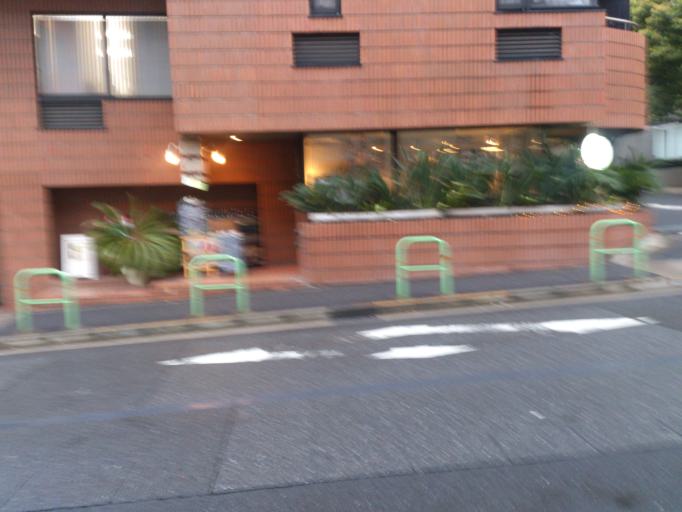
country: JP
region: Tokyo
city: Tokyo
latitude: 35.6702
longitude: 139.7378
